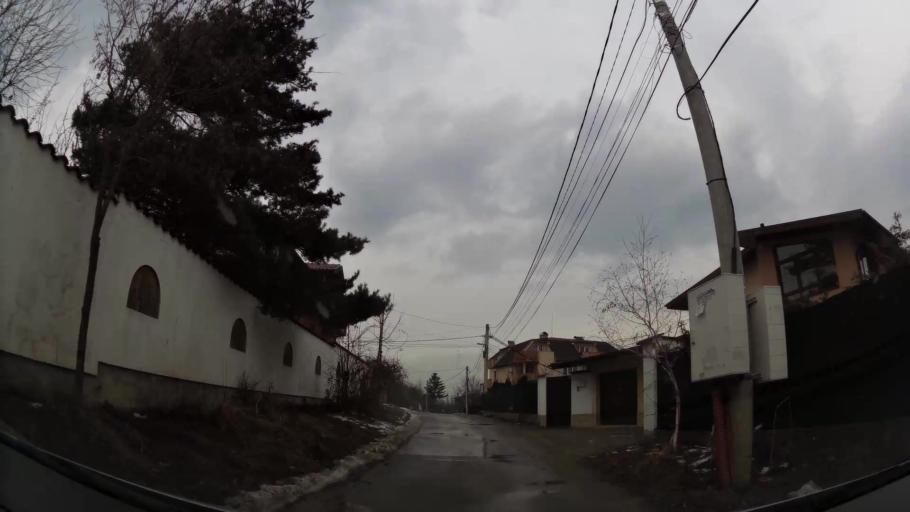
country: BG
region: Sofiya
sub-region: Obshtina Bozhurishte
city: Bozhurishte
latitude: 42.6823
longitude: 23.2344
